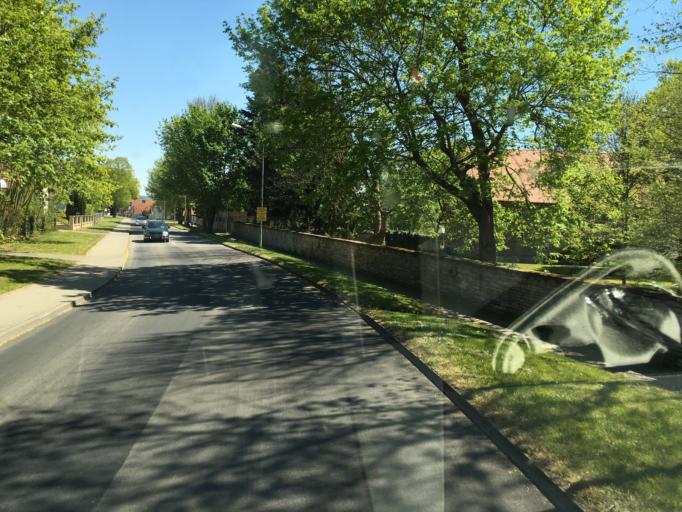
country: DE
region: Thuringia
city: Rossleben
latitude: 51.2964
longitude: 11.4265
